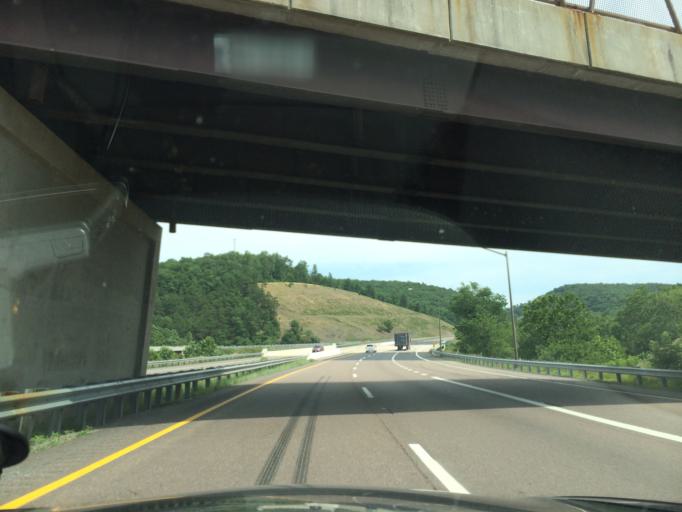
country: US
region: West Virginia
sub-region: Morgan County
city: Berkeley Springs
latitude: 39.6760
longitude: -78.4589
